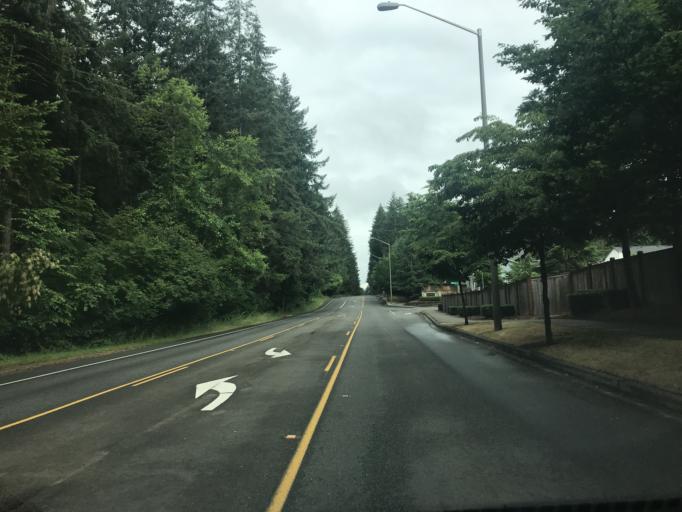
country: US
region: Washington
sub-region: King County
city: Maple Valley
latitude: 47.3436
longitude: -122.0405
